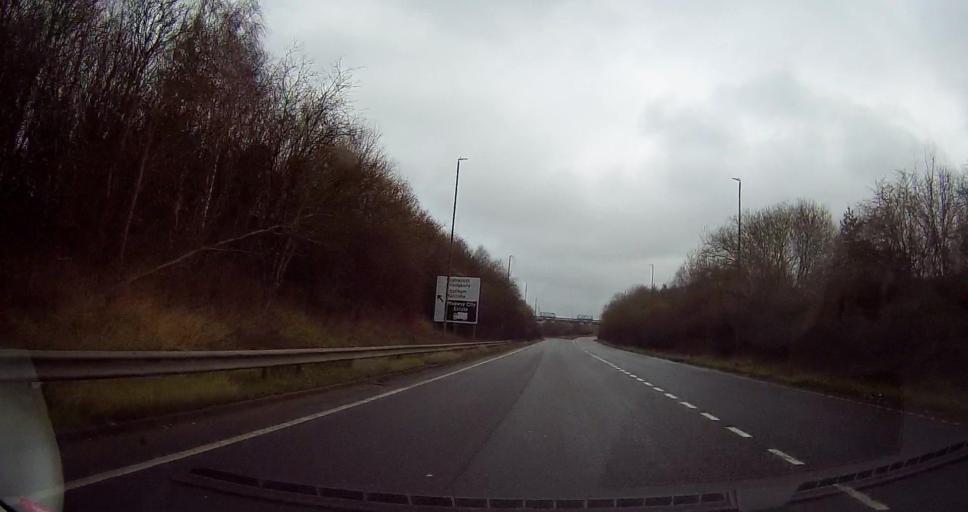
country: GB
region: England
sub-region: Medway
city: Cuxton
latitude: 51.4000
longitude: 0.4397
